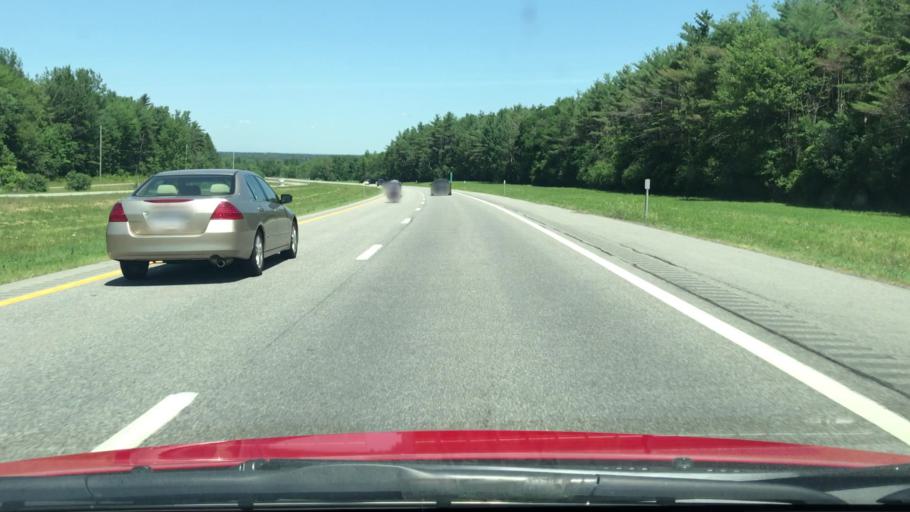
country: US
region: New York
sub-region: Essex County
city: Keeseville
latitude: 44.4597
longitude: -73.4852
